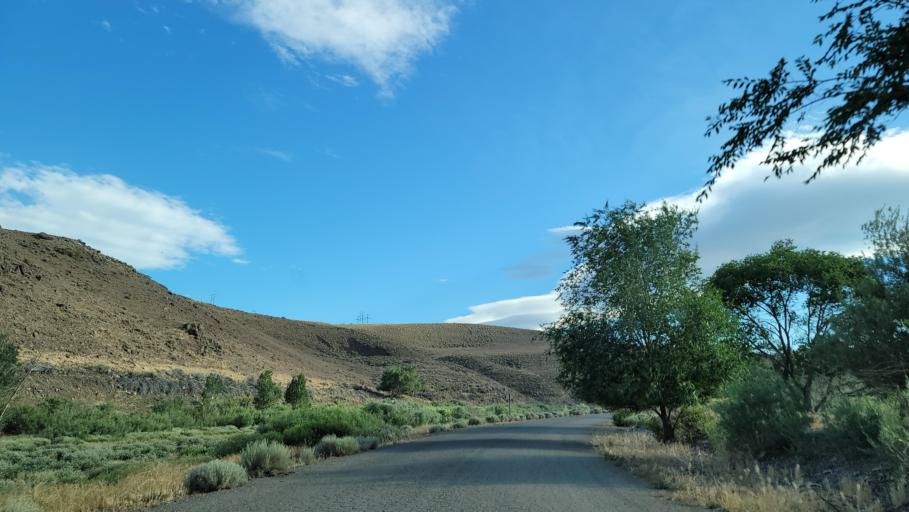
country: US
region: Nevada
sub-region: Washoe County
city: Sparks
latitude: 39.5138
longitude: -119.6190
